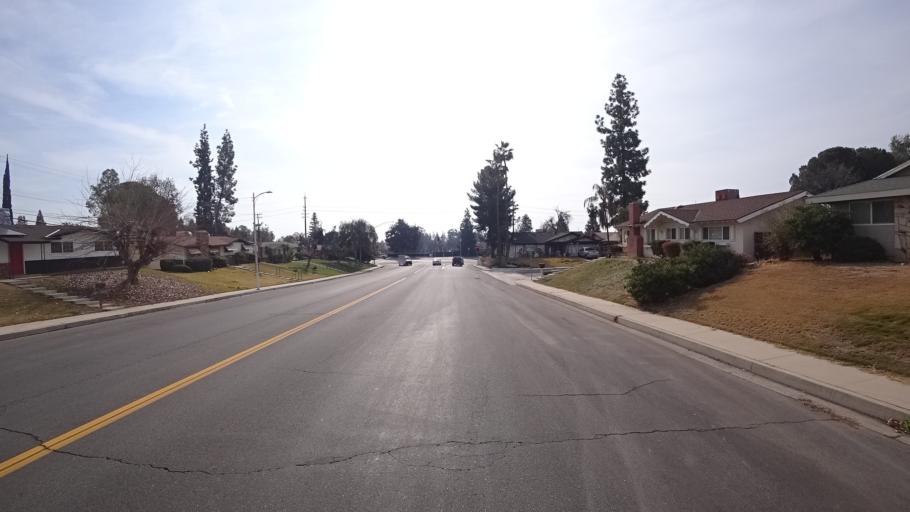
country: US
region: California
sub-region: Kern County
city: Oildale
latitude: 35.3986
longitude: -118.9587
